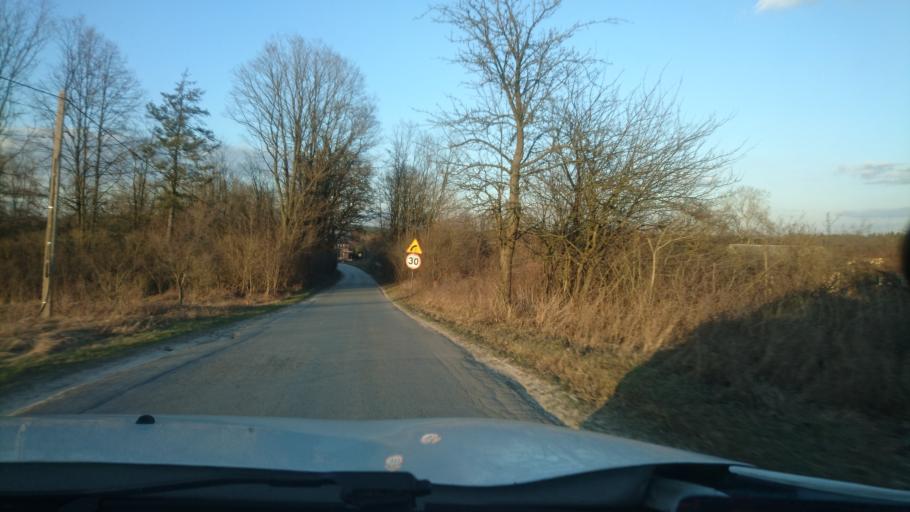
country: PL
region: Swietokrzyskie
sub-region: Powiat kielecki
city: Morawica
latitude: 50.7775
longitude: 20.7042
